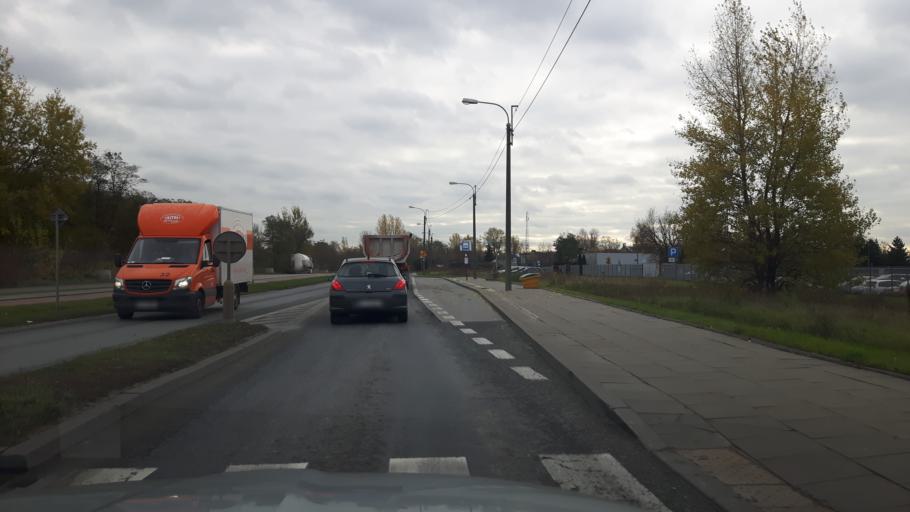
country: PL
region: Masovian Voivodeship
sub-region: Warszawa
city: Praga Poludnie
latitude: 52.2637
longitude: 21.0773
